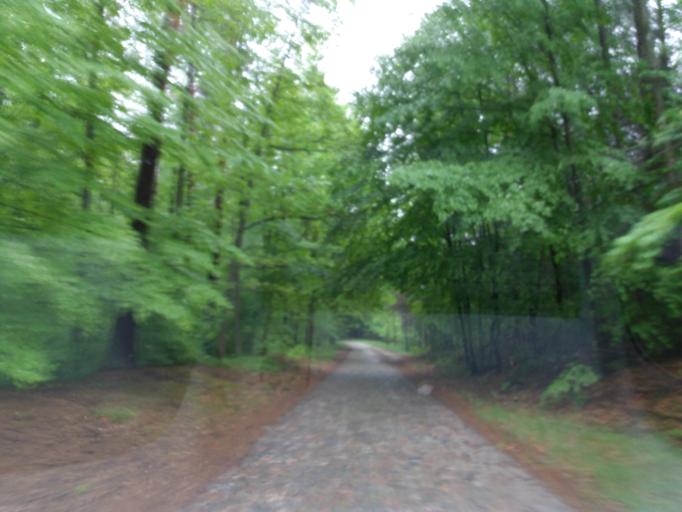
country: PL
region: Greater Poland Voivodeship
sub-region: Powiat czarnkowsko-trzcianecki
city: Krzyz Wielkopolski
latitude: 53.0336
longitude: 15.9262
